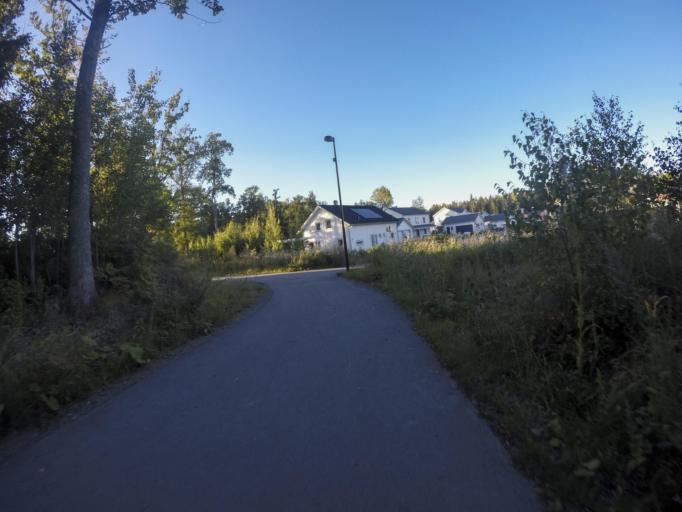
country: SE
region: Vaestmanland
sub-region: Vasteras
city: Vasteras
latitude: 59.5493
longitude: 16.6736
